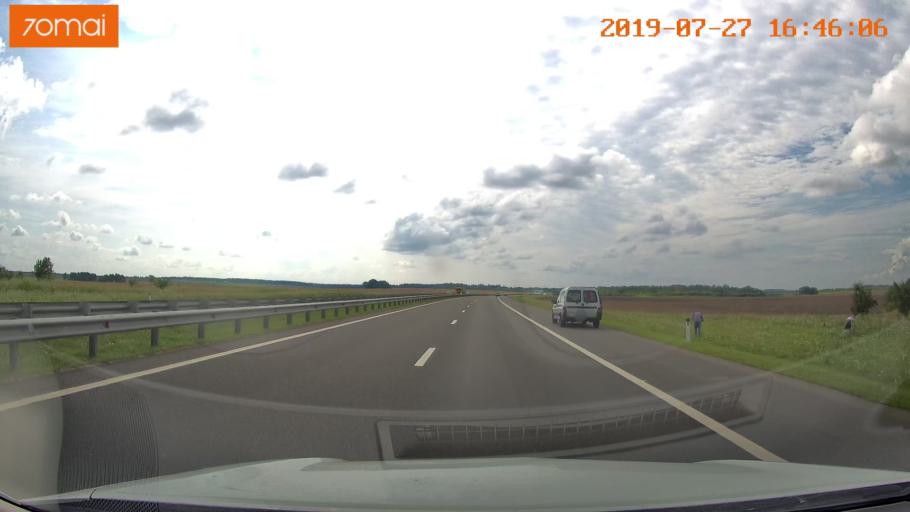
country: RU
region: Kaliningrad
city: Gvardeysk
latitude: 54.6674
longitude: 21.0311
